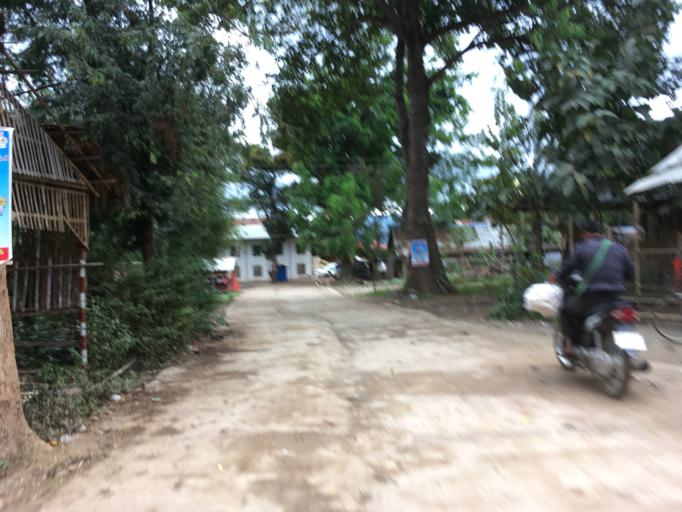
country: MM
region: Shan
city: Taunggyi
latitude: 20.6202
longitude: 96.8825
